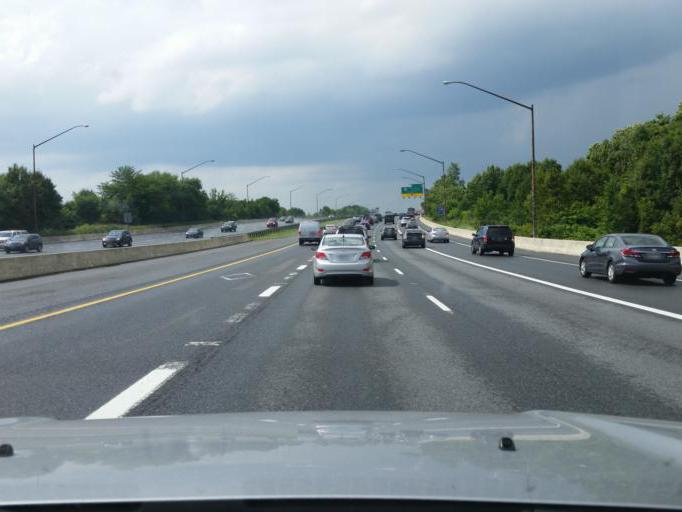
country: US
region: Maryland
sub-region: Montgomery County
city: Germantown
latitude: 39.1880
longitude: -77.2576
